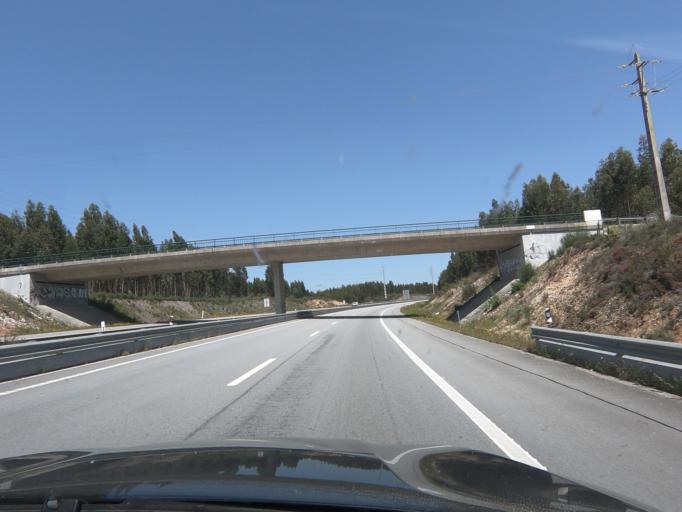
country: PT
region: Santarem
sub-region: Entroncamento
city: Entroncamento
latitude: 39.4993
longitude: -8.4376
